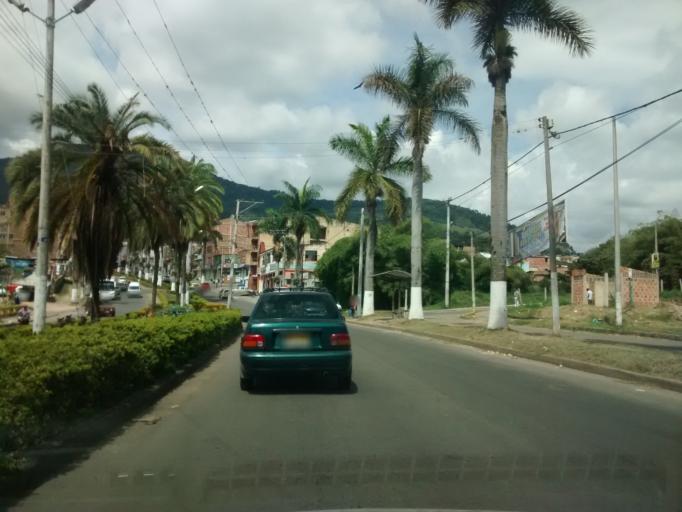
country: CO
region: Cundinamarca
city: Fusagasuga
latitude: 4.3413
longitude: -74.3672
